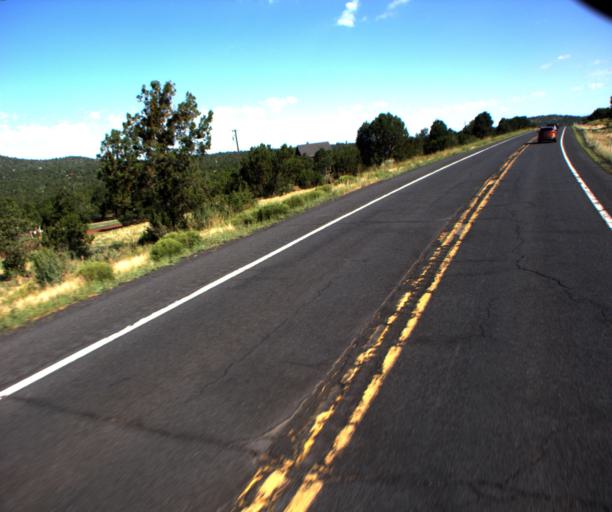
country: US
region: Arizona
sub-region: Coconino County
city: Williams
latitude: 35.3460
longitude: -112.1666
